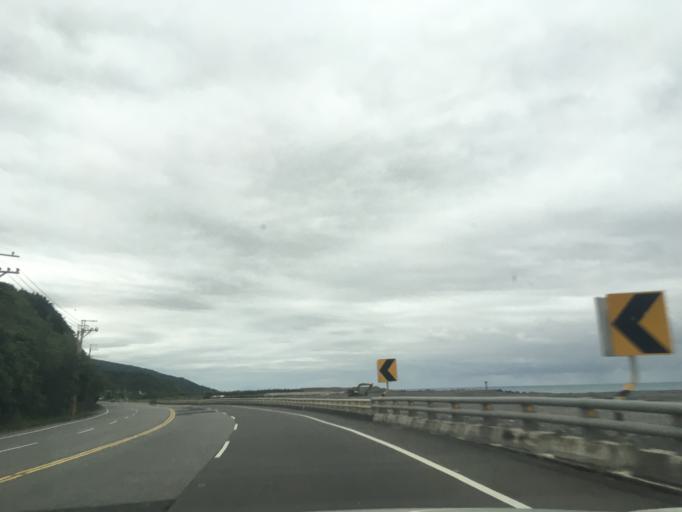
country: TW
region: Taiwan
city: Hengchun
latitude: 22.3315
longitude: 120.8929
